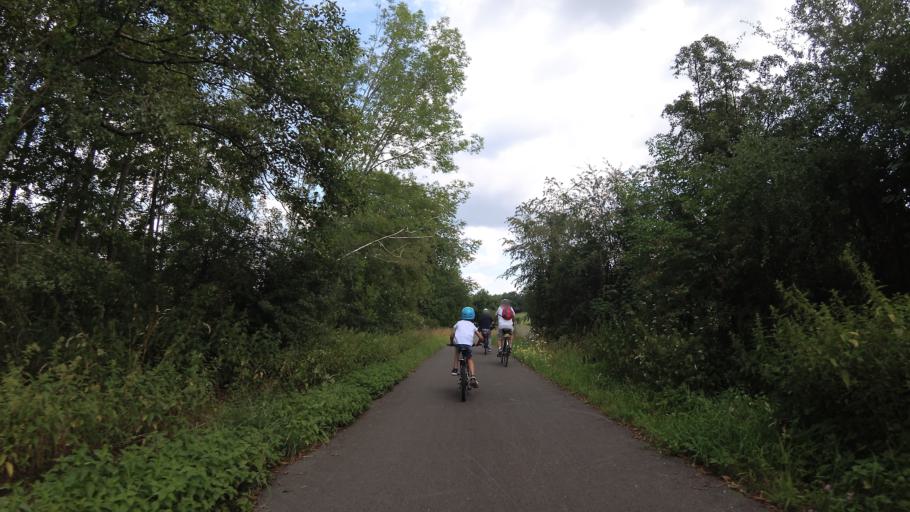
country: DE
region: Saarland
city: Blieskastel
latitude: 49.1850
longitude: 7.2482
